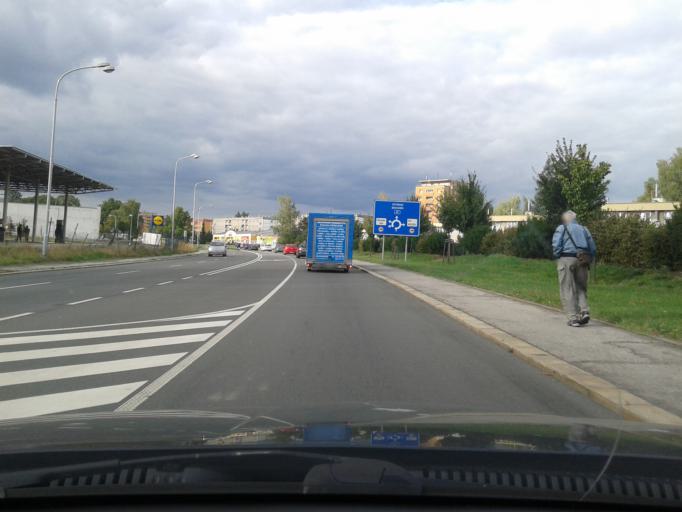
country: CZ
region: Moravskoslezsky
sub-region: Okres Karvina
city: Karvina
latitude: 49.8435
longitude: 18.5567
